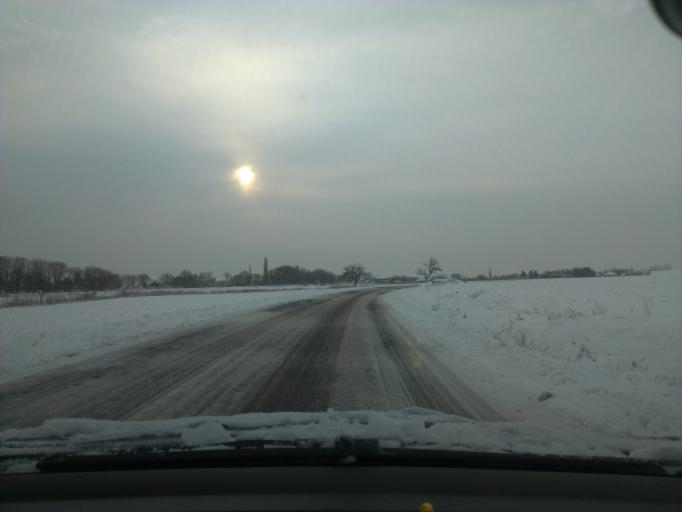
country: SK
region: Trnavsky
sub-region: Okres Trnava
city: Piestany
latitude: 48.5340
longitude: 17.9583
